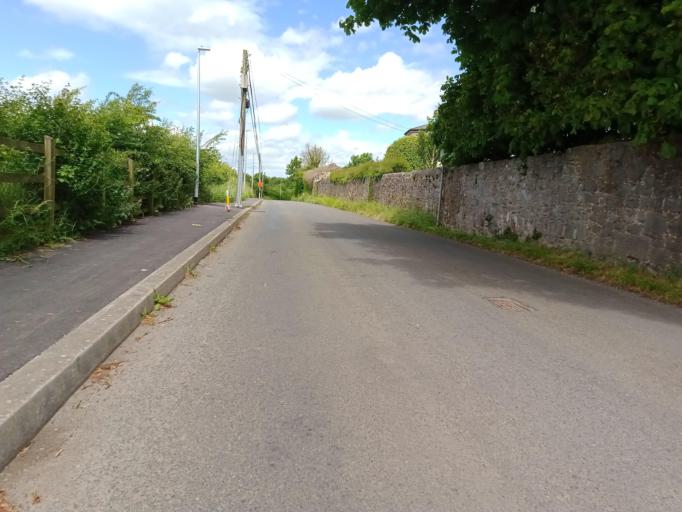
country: IE
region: Leinster
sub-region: Kilkenny
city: Kilkenny
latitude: 52.6777
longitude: -7.2491
